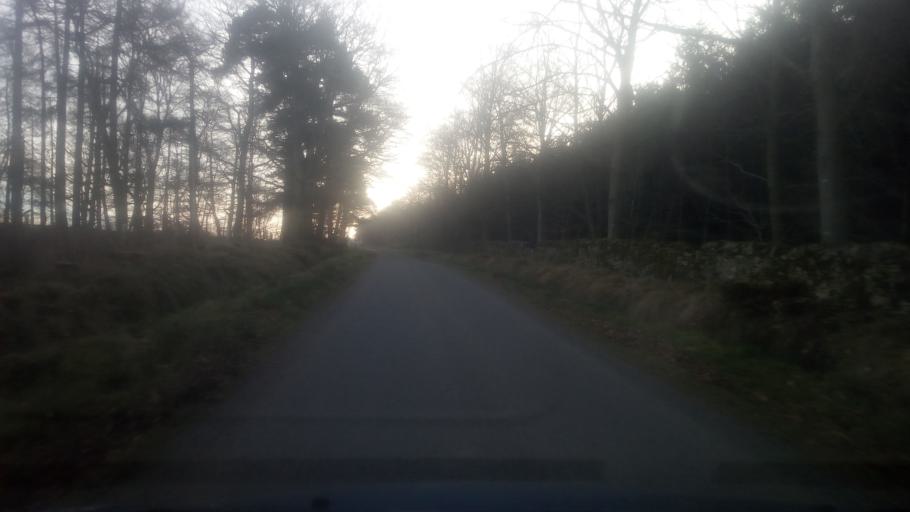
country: GB
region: Scotland
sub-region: The Scottish Borders
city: Jedburgh
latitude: 55.4260
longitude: -2.5623
